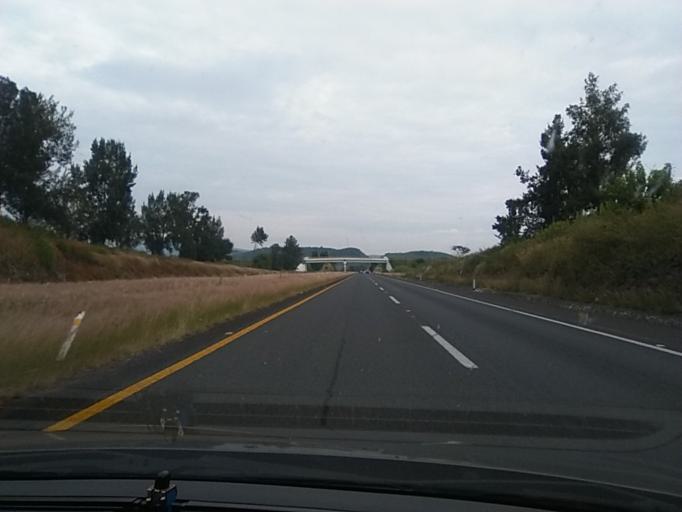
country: MX
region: Michoacan
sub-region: Puruandiro
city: San Lorenzo
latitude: 19.9520
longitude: -101.6506
